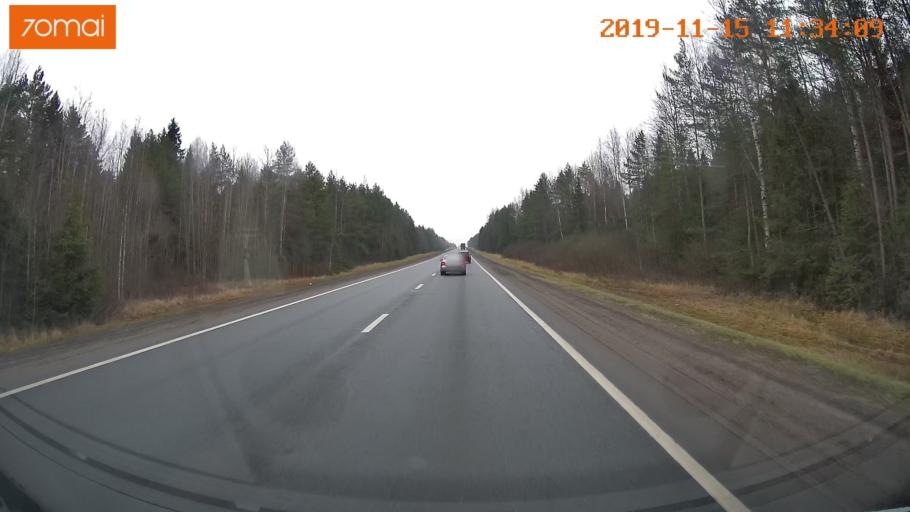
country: RU
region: Vologda
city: Molochnoye
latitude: 59.1921
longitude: 39.6062
